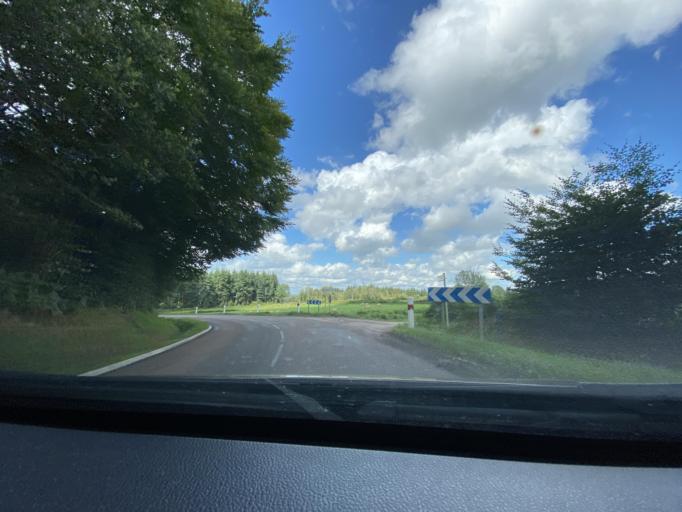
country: FR
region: Bourgogne
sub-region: Departement de la Cote-d'Or
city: Saulieu
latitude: 47.2589
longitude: 4.1261
